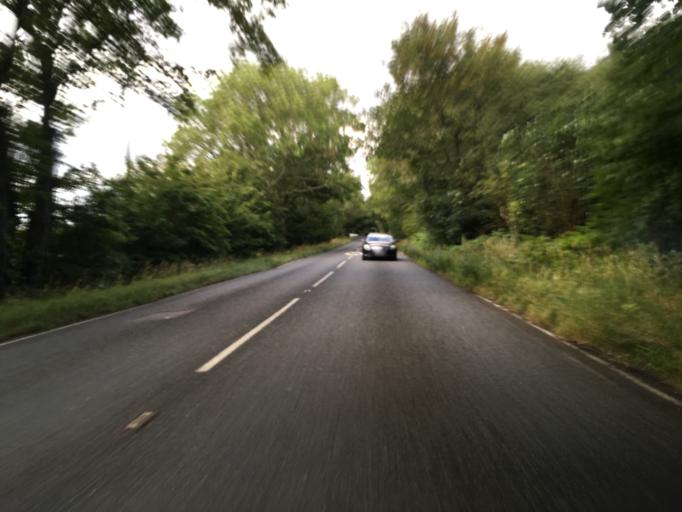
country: GB
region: England
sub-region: Hampshire
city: Kings Worthy
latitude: 51.1459
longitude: -1.2471
